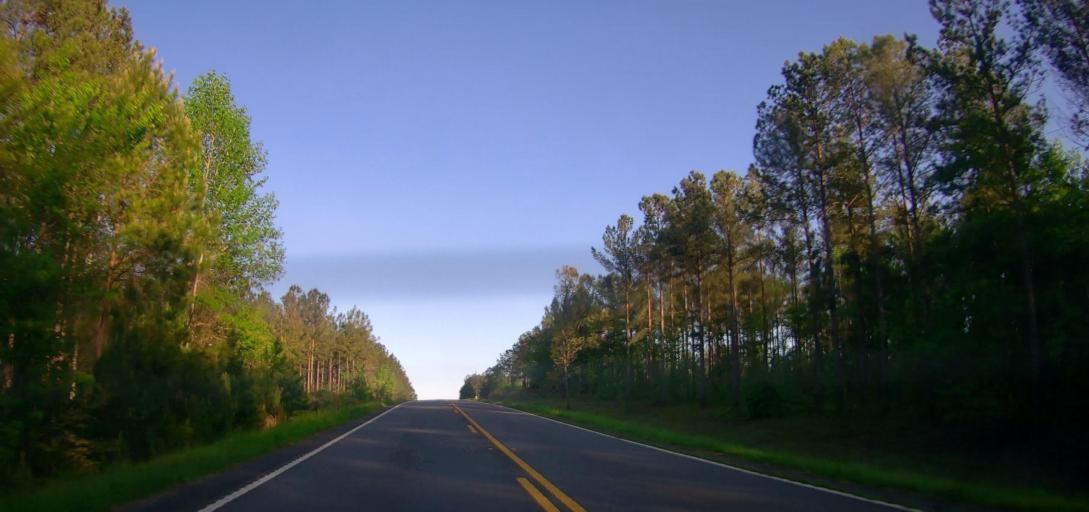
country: US
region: Georgia
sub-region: Schley County
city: Ellaville
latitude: 32.3523
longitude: -84.3812
